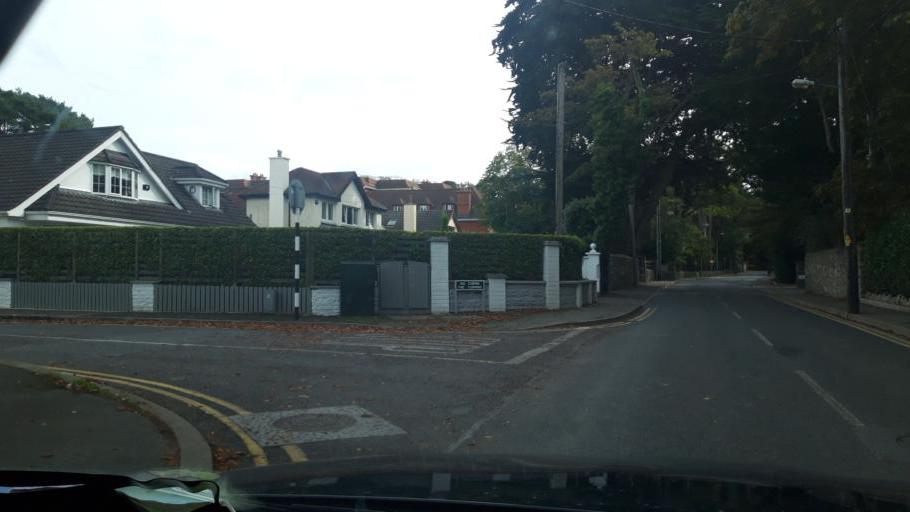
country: IE
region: Leinster
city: Foxrock
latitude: 53.2649
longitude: -6.1825
